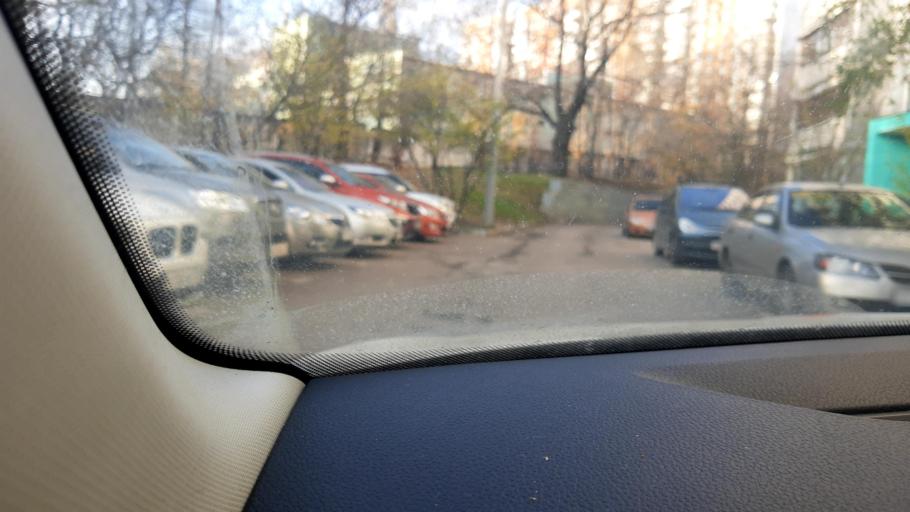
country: RU
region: Moscow
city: Chertanovo Yuzhnoye
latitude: 55.5885
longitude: 37.5946
